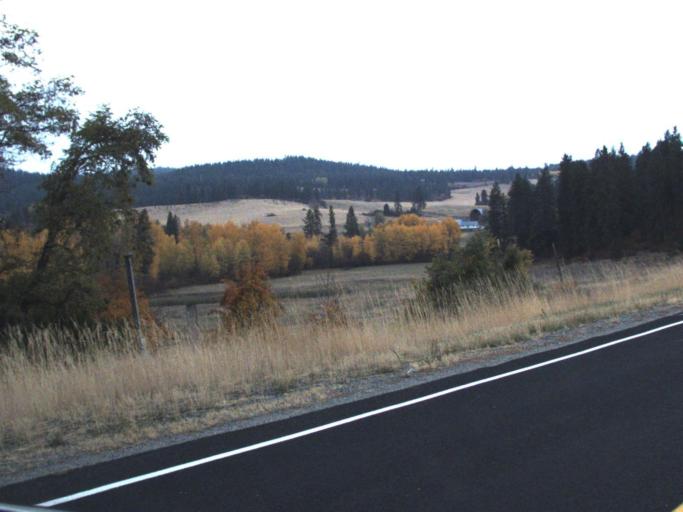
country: US
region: Washington
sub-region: Lincoln County
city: Davenport
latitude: 48.0033
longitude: -118.2738
